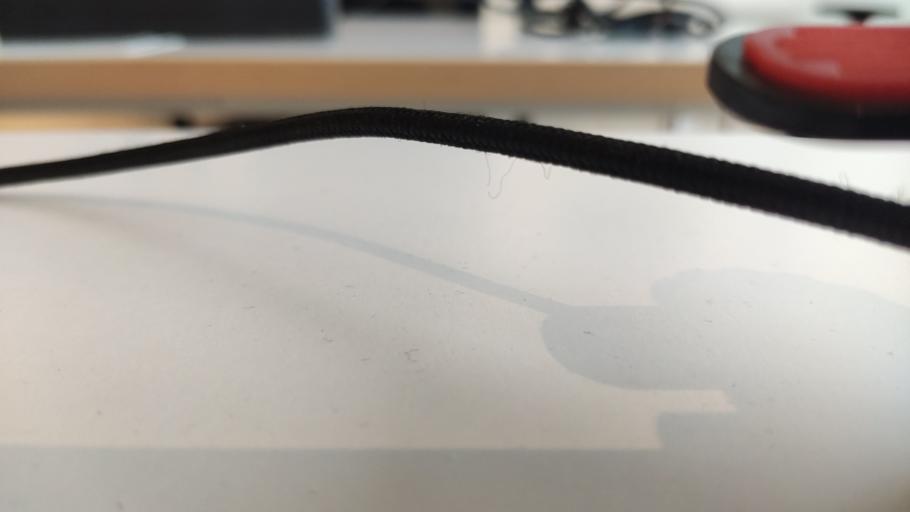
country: RU
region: Moskovskaya
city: Klin
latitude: 56.3387
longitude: 36.7403
